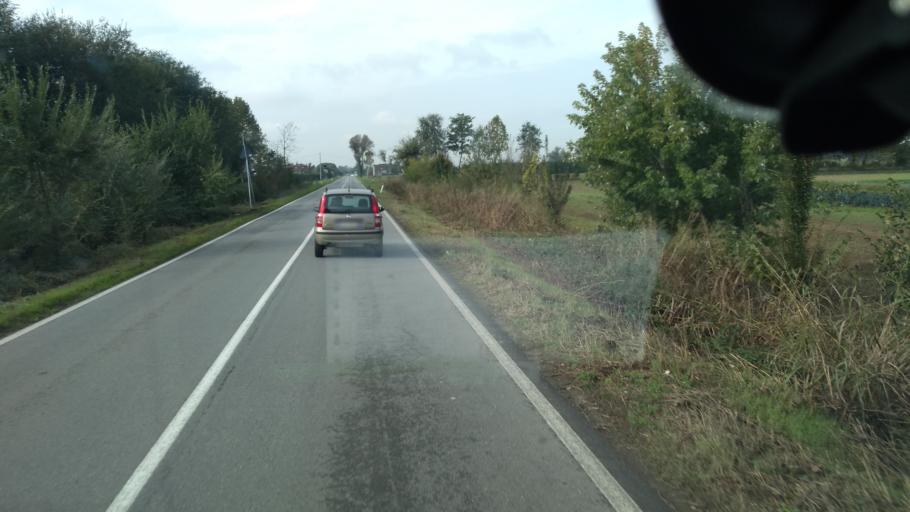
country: IT
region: Lombardy
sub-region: Provincia di Bergamo
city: Brignano Gera d'Adda
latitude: 45.5524
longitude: 9.6534
